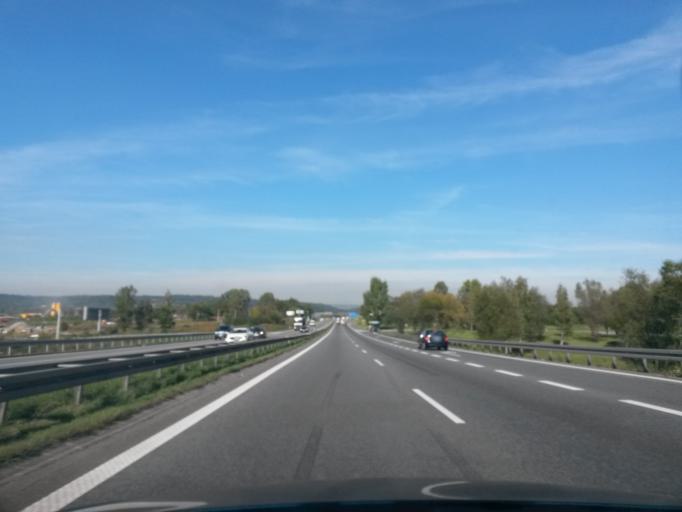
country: PL
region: Lesser Poland Voivodeship
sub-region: Powiat krakowski
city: Balice
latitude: 50.0728
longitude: 19.8102
